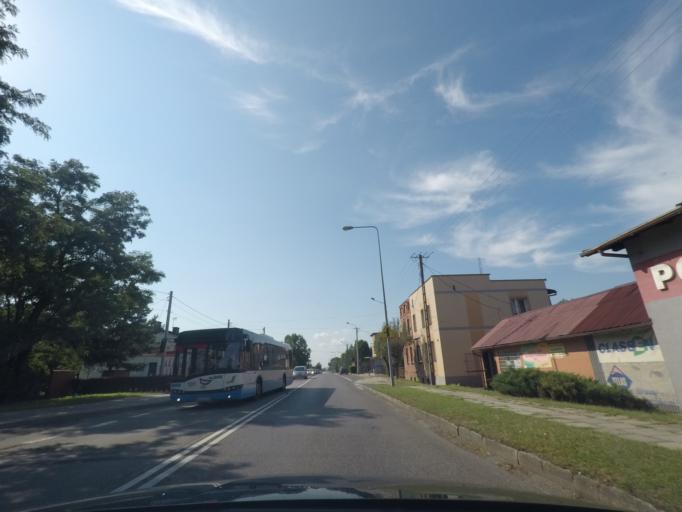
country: PL
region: Silesian Voivodeship
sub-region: Zory
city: Zory
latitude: 50.0515
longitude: 18.6862
